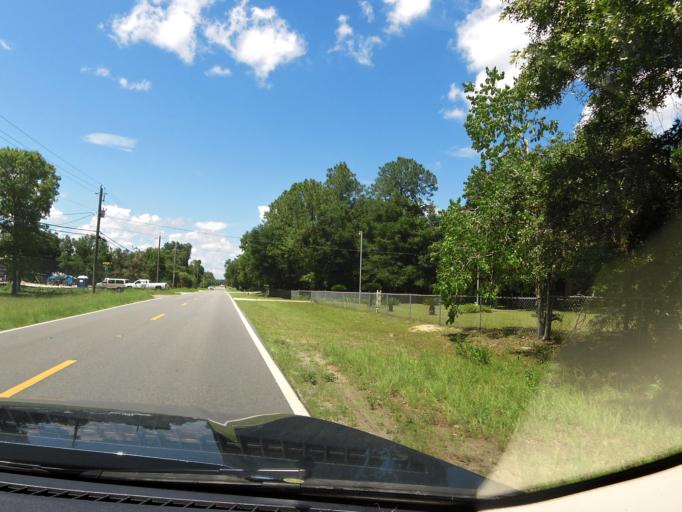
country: US
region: Georgia
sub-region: Camden County
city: St. Marys
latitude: 30.6636
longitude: -81.5416
